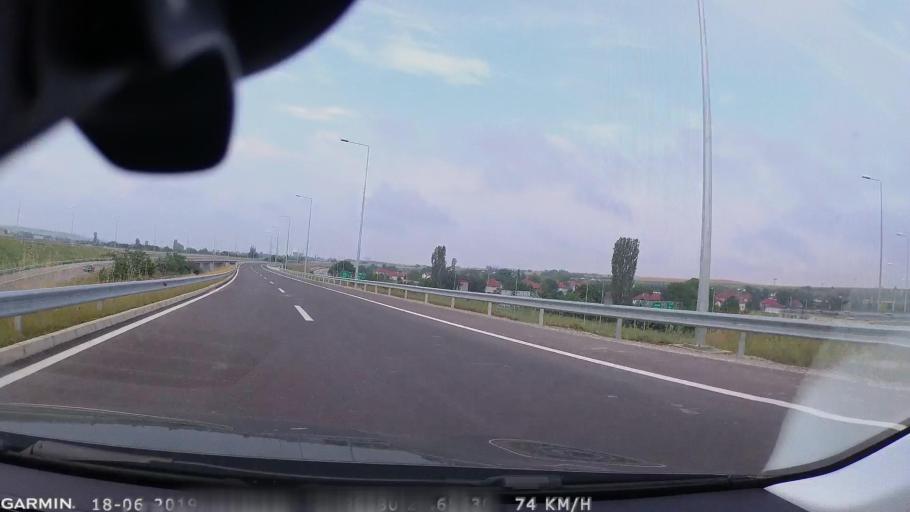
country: MK
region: Petrovec
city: Sredno Konjare
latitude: 41.9508
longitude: 21.7612
